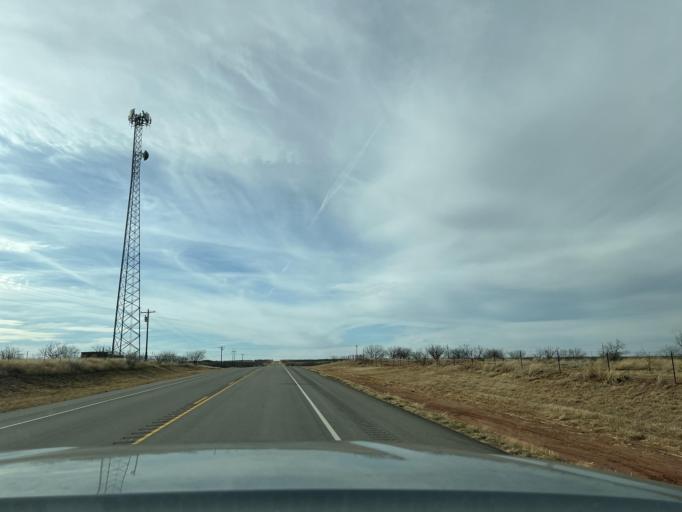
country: US
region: Texas
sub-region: Jones County
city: Anson
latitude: 32.7508
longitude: -99.7241
